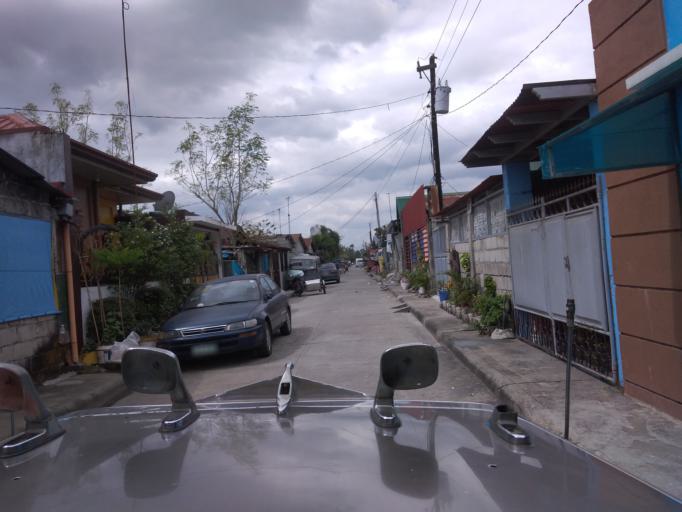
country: PH
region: Central Luzon
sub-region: Province of Pampanga
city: Pandacaqui
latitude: 15.1786
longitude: 120.6566
